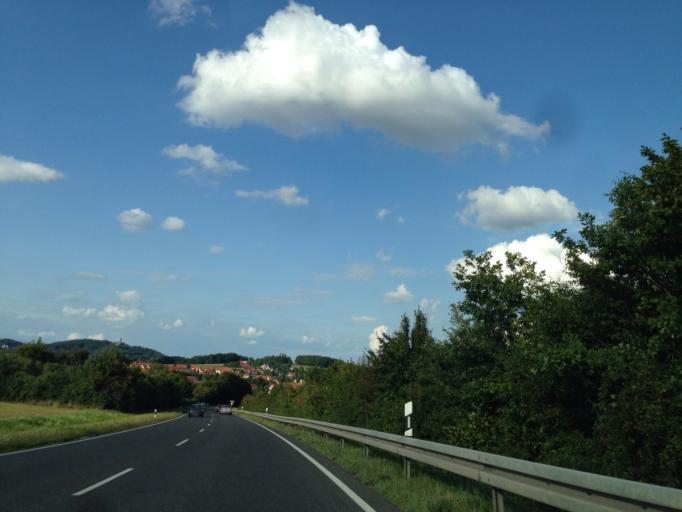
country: DE
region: Bavaria
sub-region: Upper Franconia
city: Stegaurach
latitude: 49.8531
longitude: 10.8519
